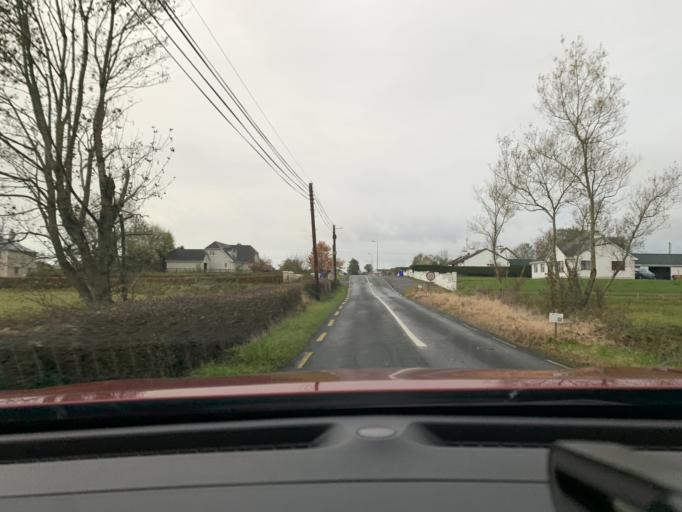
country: IE
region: Connaught
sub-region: Sligo
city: Ballymote
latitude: 53.9999
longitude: -8.5204
